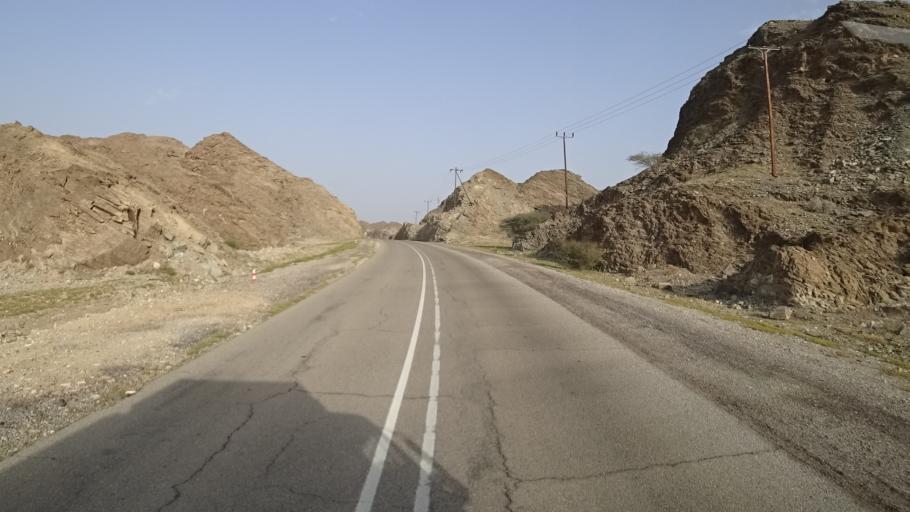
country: OM
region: Muhafazat Masqat
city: Bawshar
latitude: 23.3584
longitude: 58.5275
